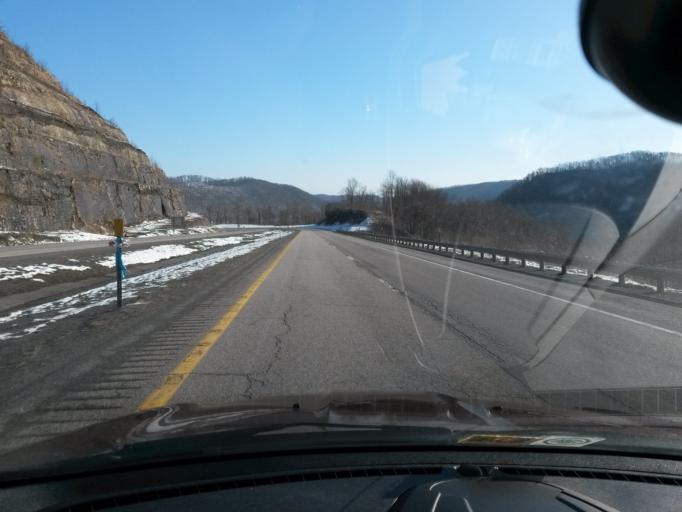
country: US
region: West Virginia
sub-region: Nicholas County
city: Craigsville
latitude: 38.4662
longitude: -80.7815
